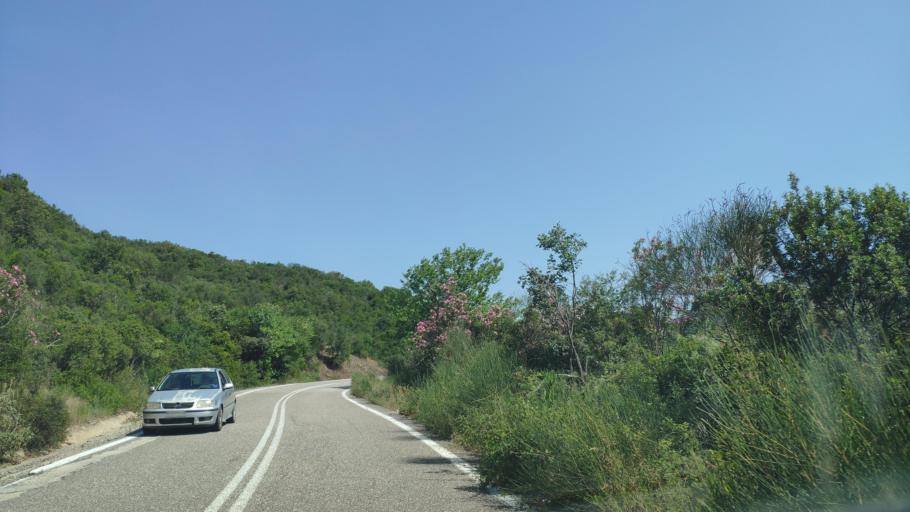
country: GR
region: West Greece
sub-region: Nomos Aitolias kai Akarnanias
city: Lepenou
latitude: 38.7646
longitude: 21.3373
